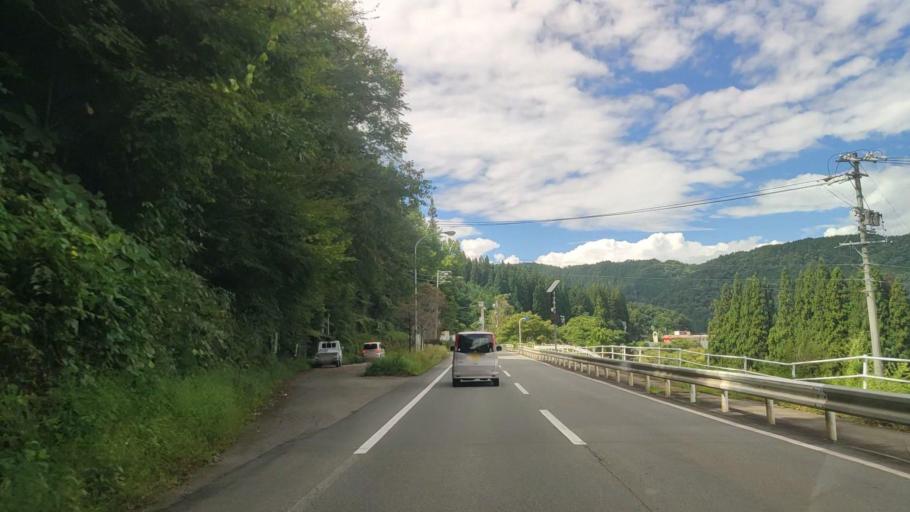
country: JP
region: Gifu
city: Takayama
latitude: 36.1808
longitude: 137.2606
